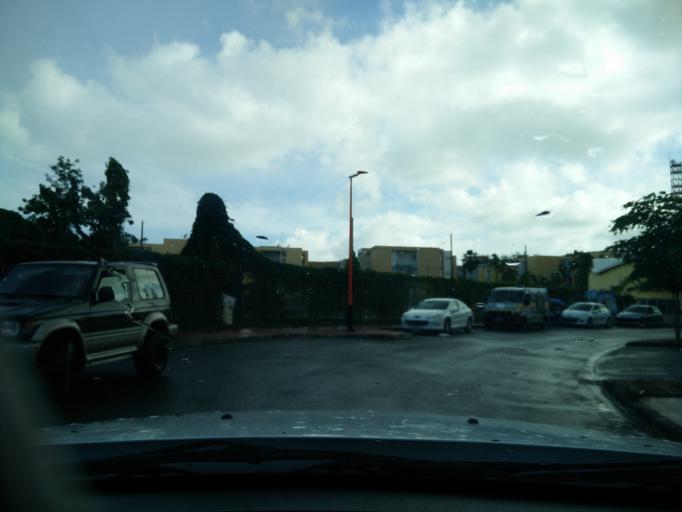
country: GP
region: Guadeloupe
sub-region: Guadeloupe
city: Pointe-a-Pitre
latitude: 16.2508
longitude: -61.5349
